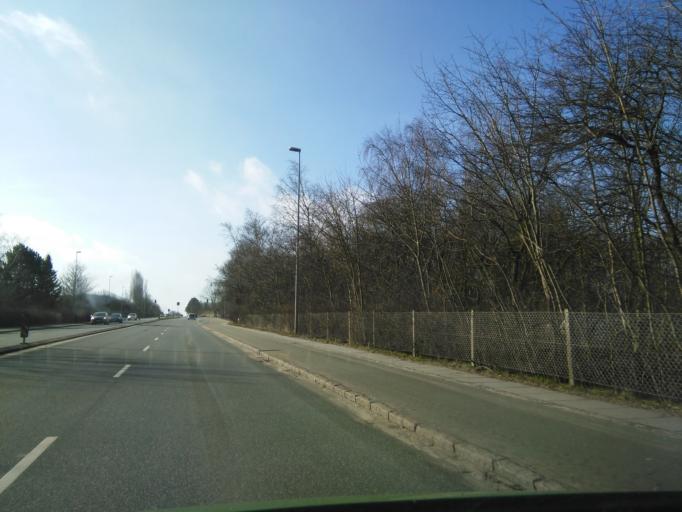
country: DK
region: Central Jutland
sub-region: Arhus Kommune
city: Tranbjerg
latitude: 56.1094
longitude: 10.1524
